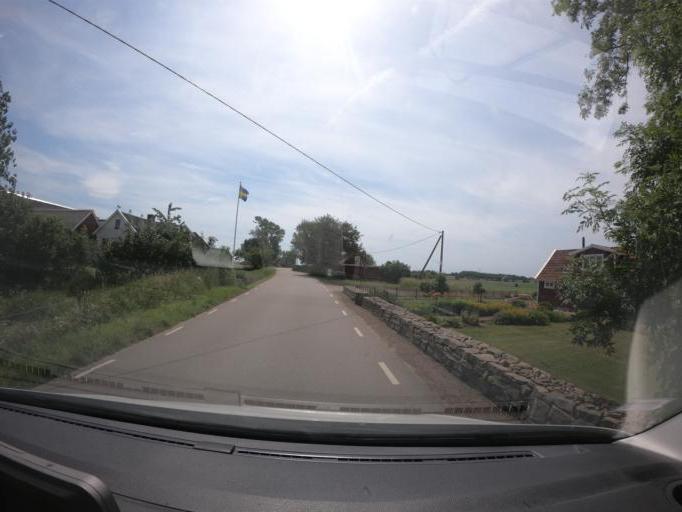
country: SE
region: Skane
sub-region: Angelholms Kommun
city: Vejbystrand
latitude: 56.3977
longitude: 12.7204
